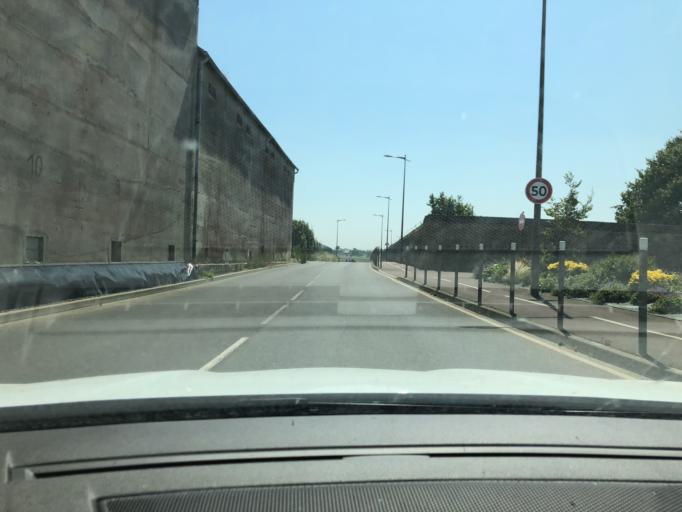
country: FR
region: Lower Normandy
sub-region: Departement du Calvados
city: Cresserons
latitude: 49.2948
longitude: -0.3663
